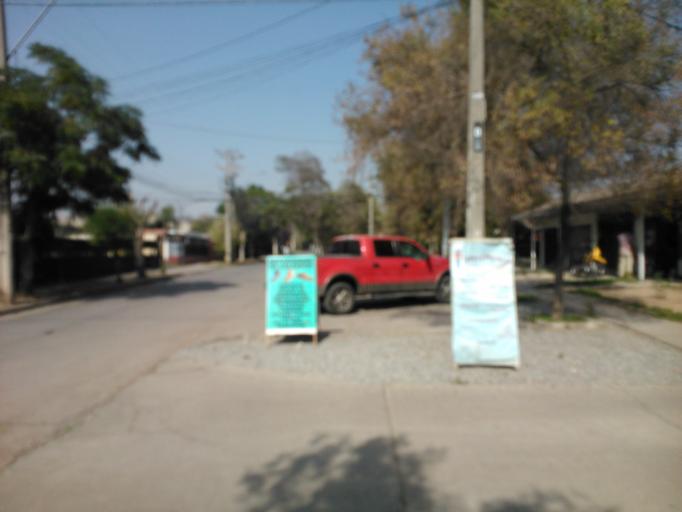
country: CL
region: Santiago Metropolitan
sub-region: Provincia de Cordillera
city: Puente Alto
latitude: -33.5565
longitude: -70.5835
